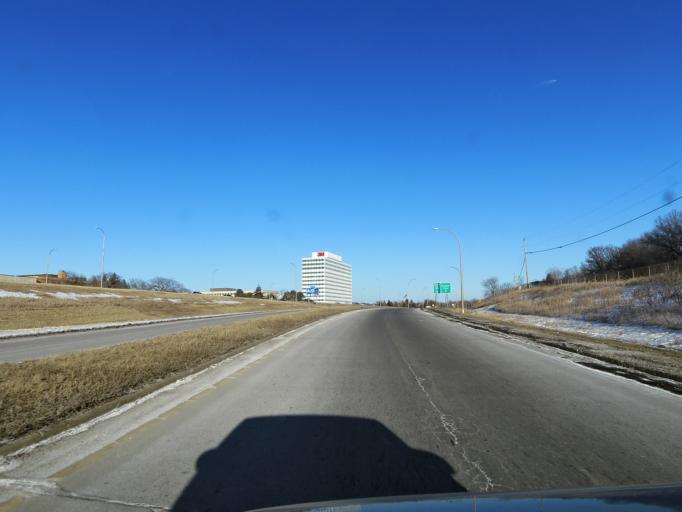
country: US
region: Minnesota
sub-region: Ramsey County
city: Maplewood
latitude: 44.9489
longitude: -93.0030
